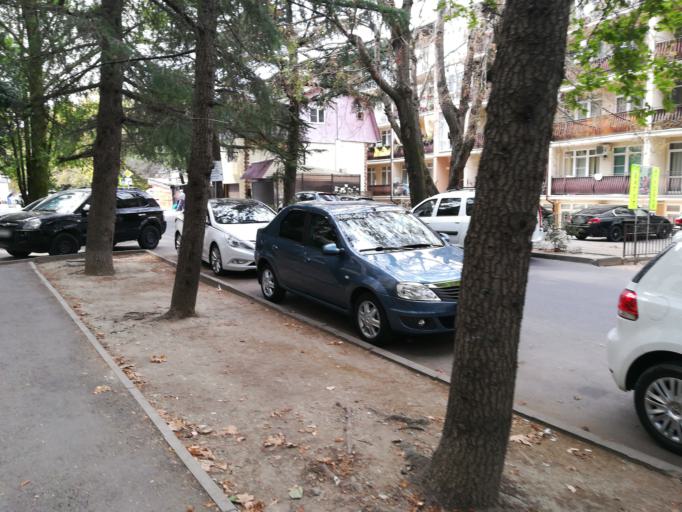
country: RU
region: Krasnodarskiy
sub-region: Sochi City
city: Sochi
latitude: 43.5930
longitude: 39.7390
